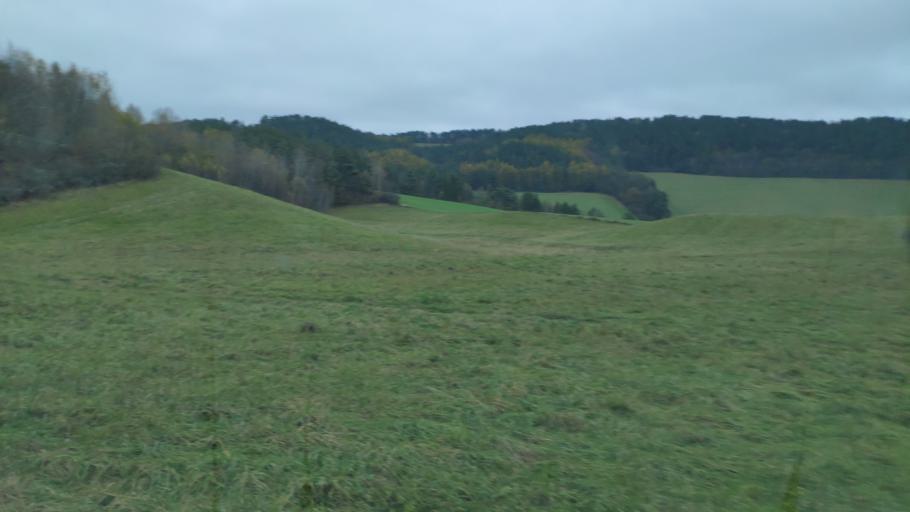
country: SK
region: Presovsky
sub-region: Okres Presov
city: Presov
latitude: 48.9276
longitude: 21.1019
